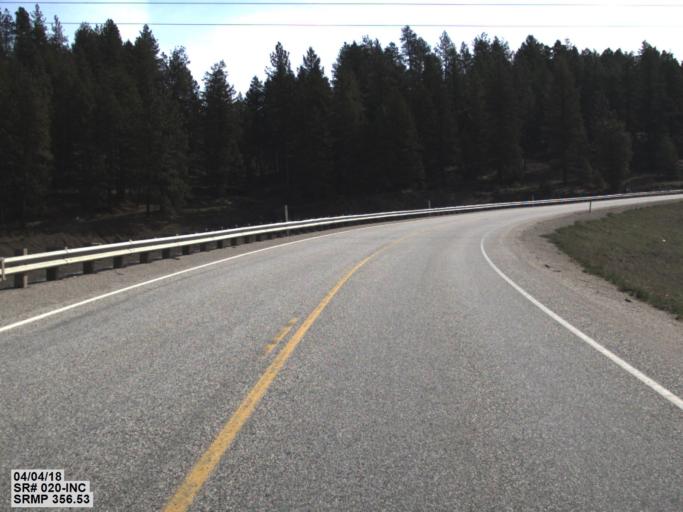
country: US
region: Washington
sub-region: Stevens County
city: Colville
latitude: 48.5475
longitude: -117.8588
